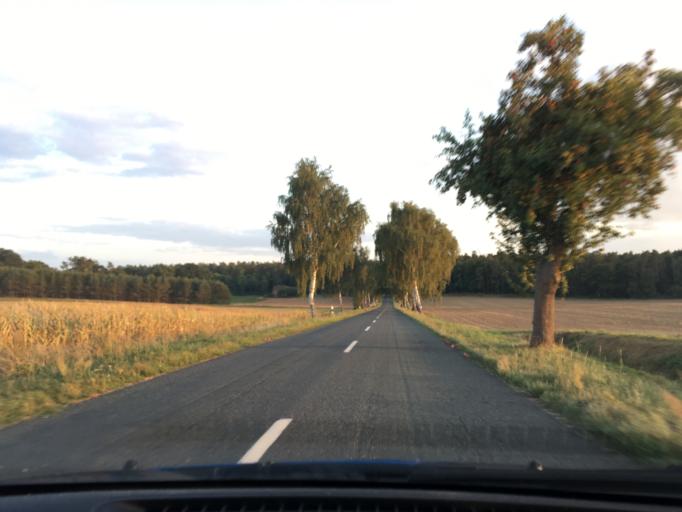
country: DE
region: Lower Saxony
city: Tosterglope
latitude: 53.2028
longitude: 10.8175
